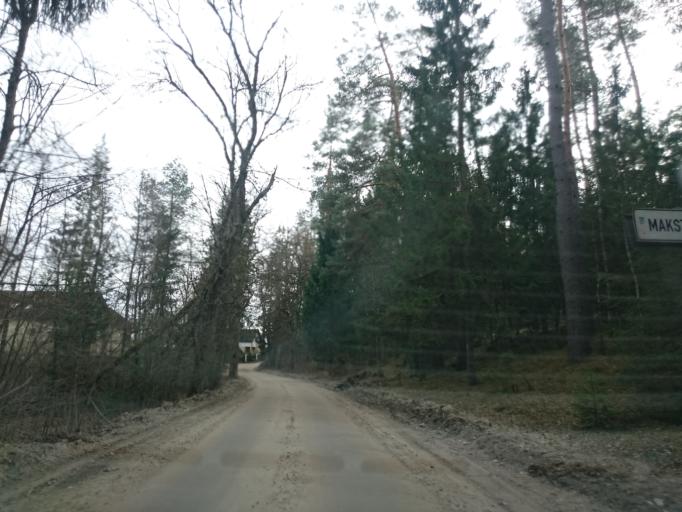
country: LV
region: Garkalne
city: Garkalne
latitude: 57.0223
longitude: 24.3868
